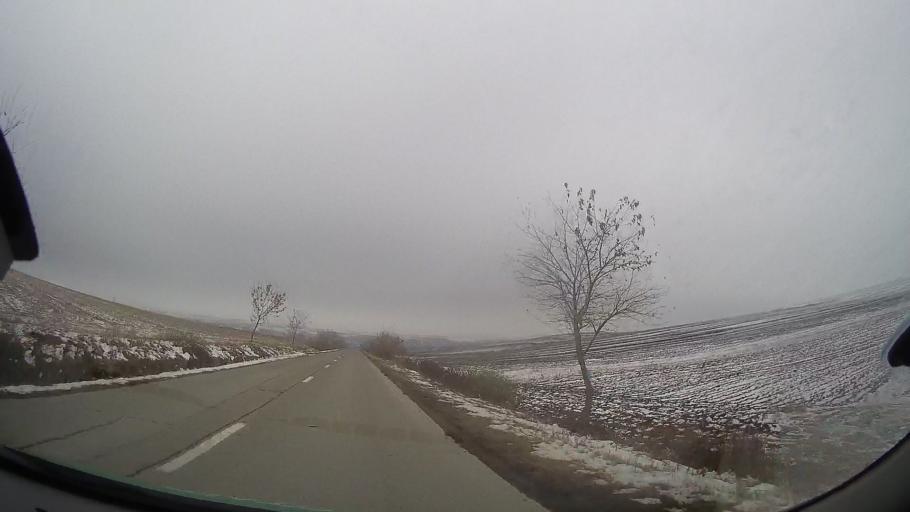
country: RO
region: Vaslui
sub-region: Comuna Ivesti
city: Ivesti
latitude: 46.1978
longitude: 27.5156
